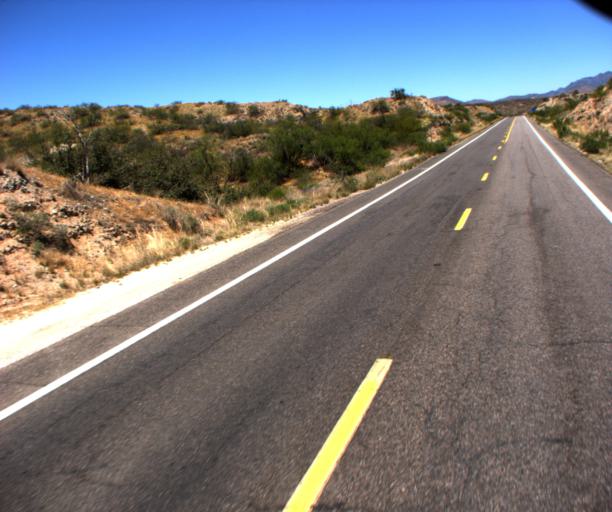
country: US
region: Arizona
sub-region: Gila County
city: Globe
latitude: 33.3605
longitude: -110.7360
